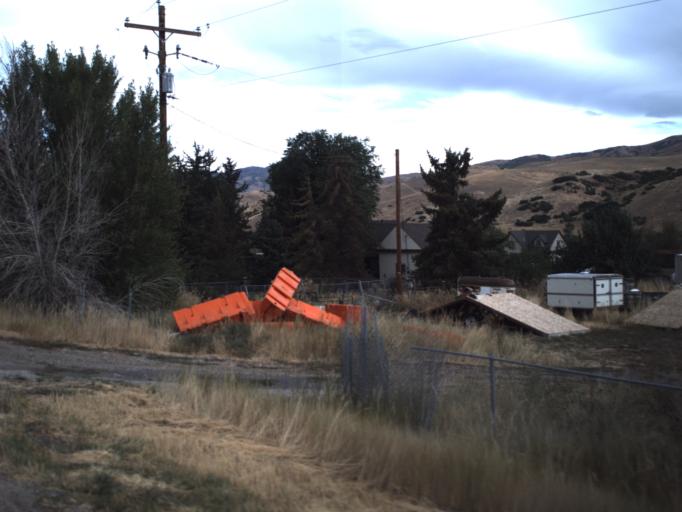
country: US
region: Utah
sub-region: Morgan County
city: Morgan
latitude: 40.9567
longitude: -111.6662
